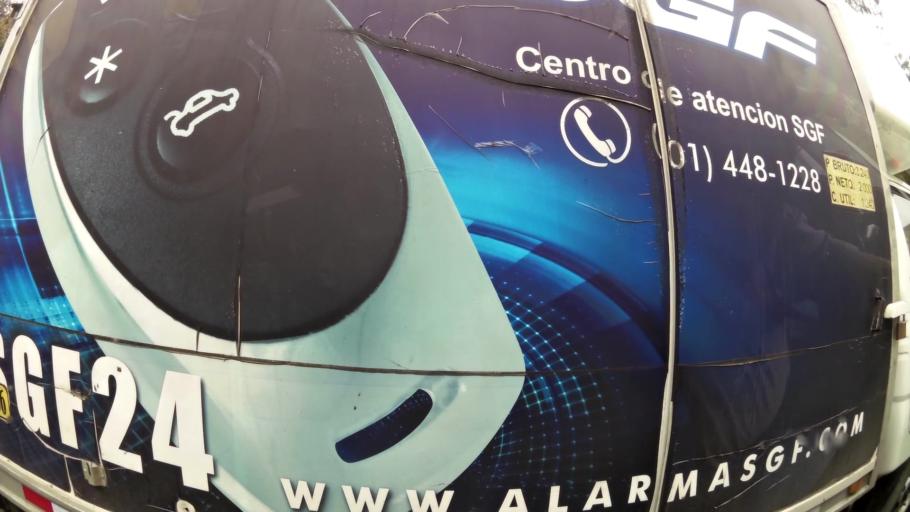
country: PE
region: Lima
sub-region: Lima
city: Surco
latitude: -12.1344
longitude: -76.9966
